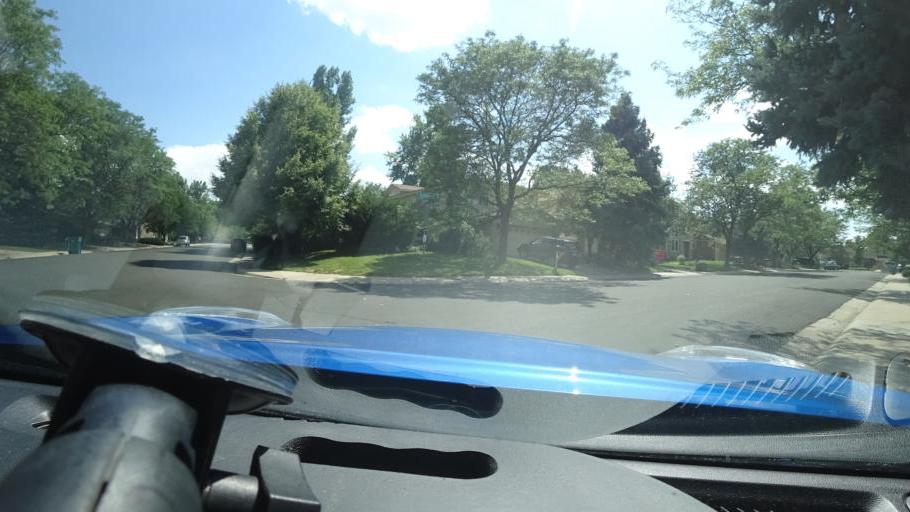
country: US
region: Colorado
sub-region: Adams County
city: Aurora
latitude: 39.6796
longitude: -104.8501
